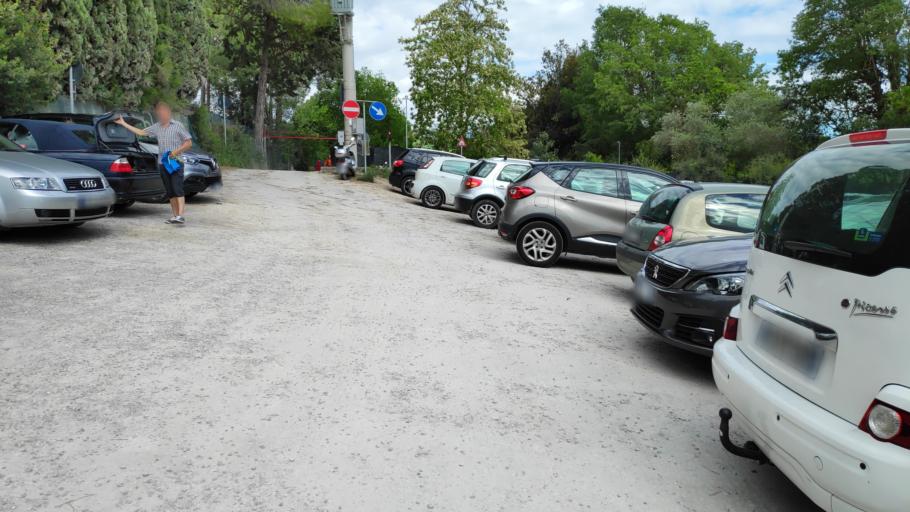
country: IT
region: Tuscany
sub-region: Provincia di Grosseto
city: Manciano
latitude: 42.6482
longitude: 11.5108
